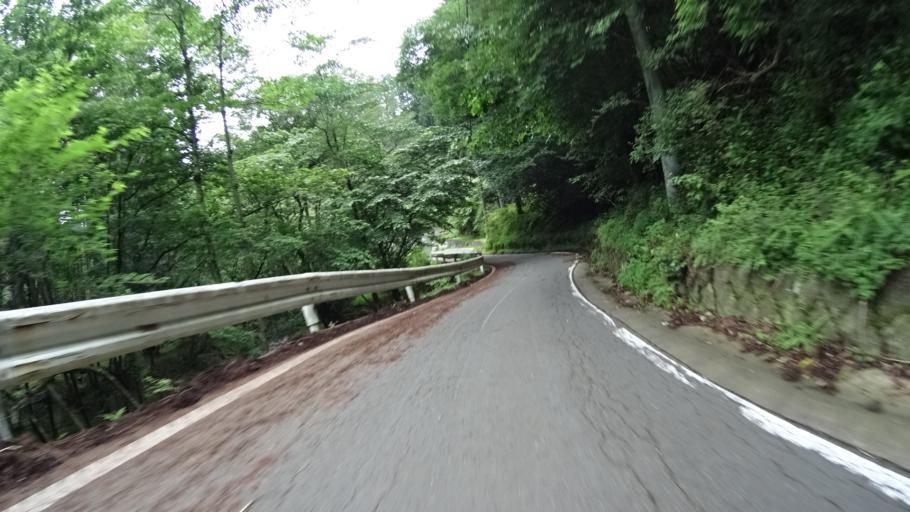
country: JP
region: Kanagawa
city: Hadano
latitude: 35.4359
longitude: 139.2118
